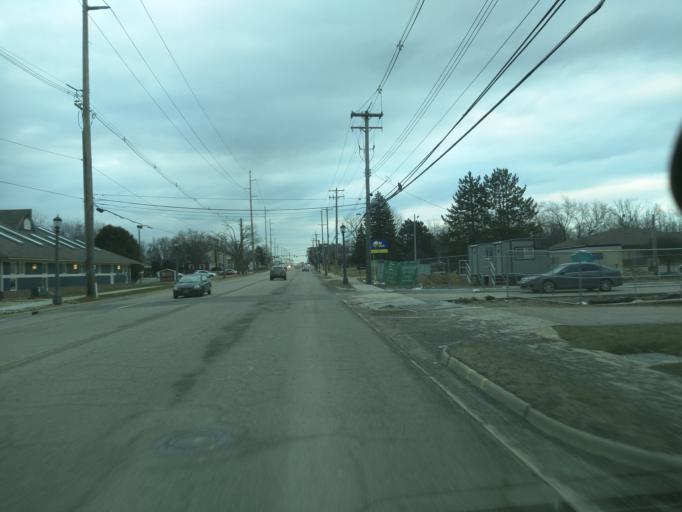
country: US
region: Michigan
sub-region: Ingham County
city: Lansing
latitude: 42.7607
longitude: -84.5269
